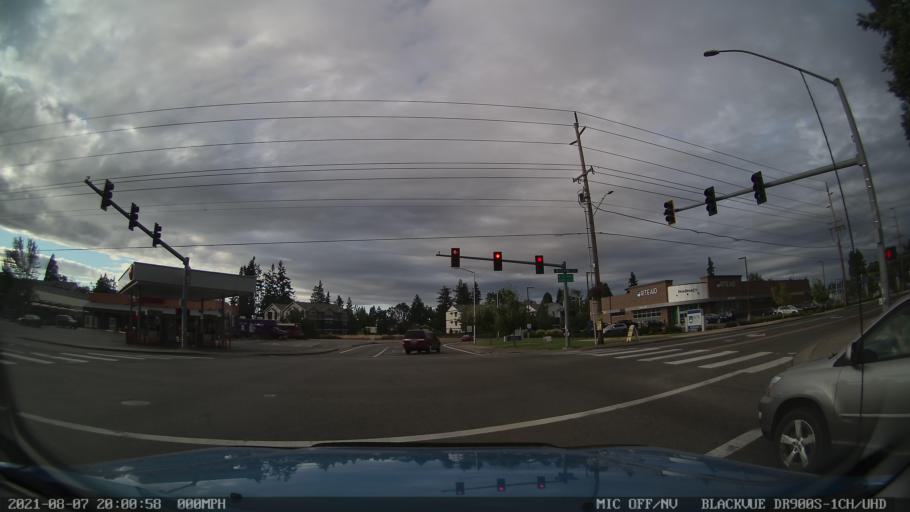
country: US
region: Oregon
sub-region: Marion County
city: Silverton
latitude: 45.0060
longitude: -122.7921
